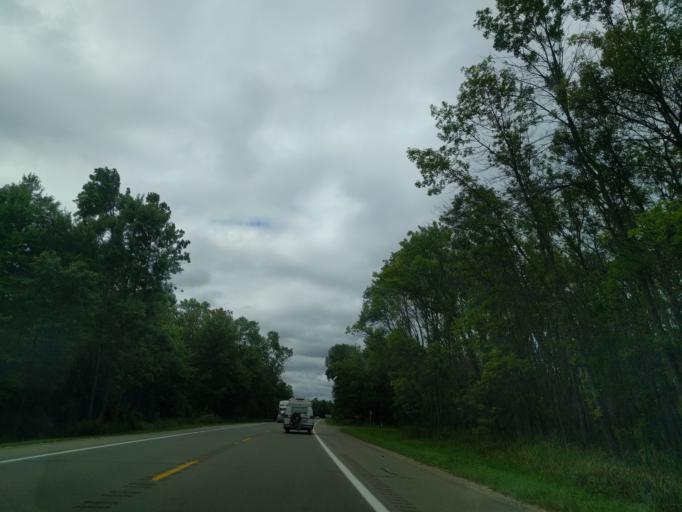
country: US
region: Michigan
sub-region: Menominee County
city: Menominee
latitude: 45.2814
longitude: -87.4566
